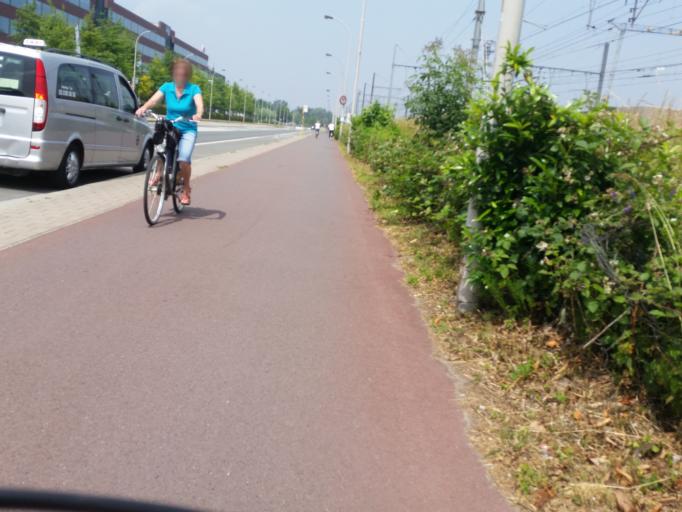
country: BE
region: Flanders
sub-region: Provincie Antwerpen
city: Mortsel
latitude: 51.1893
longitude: 4.4407
